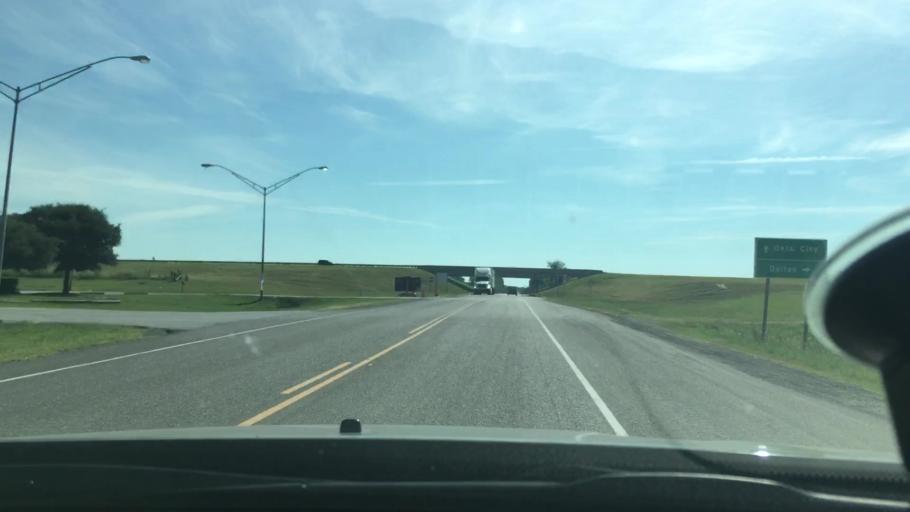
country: US
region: Oklahoma
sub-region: Carter County
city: Ardmore
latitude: 34.3327
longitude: -97.1554
